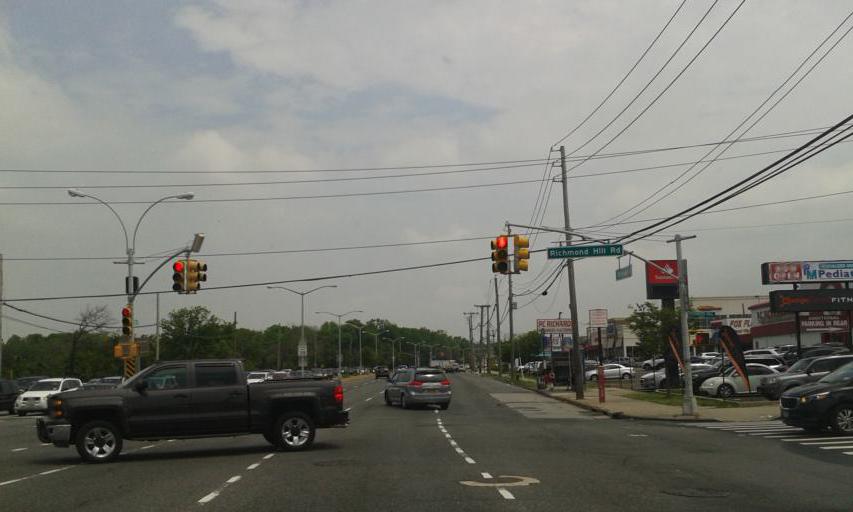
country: US
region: New York
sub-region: Richmond County
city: Bloomfield
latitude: 40.5888
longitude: -74.1676
